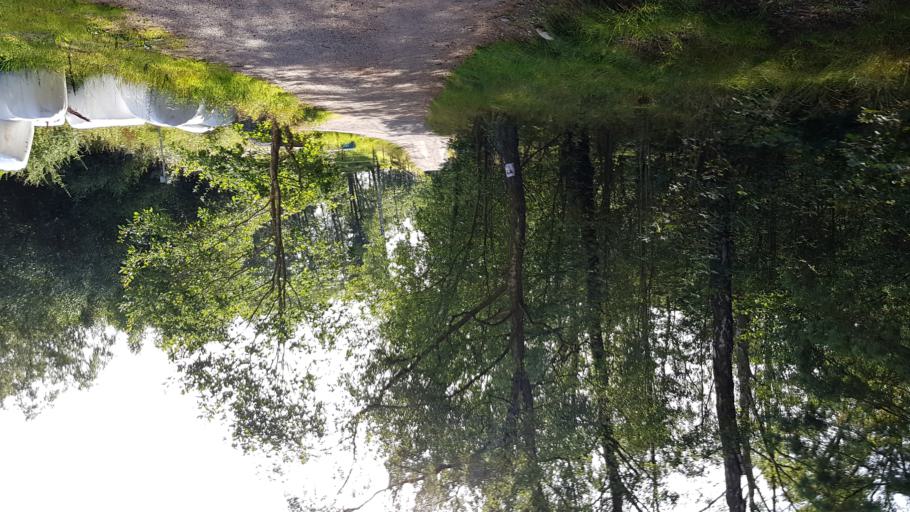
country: SE
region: Vaestra Goetaland
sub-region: Molndal
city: Moelndal
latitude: 57.6829
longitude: 12.0289
